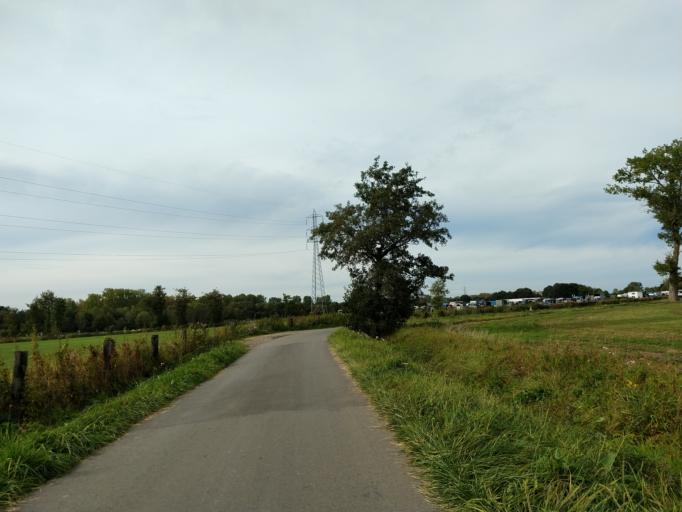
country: BE
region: Flanders
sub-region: Provincie Vlaams-Brabant
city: Haacht
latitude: 50.9664
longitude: 4.6676
